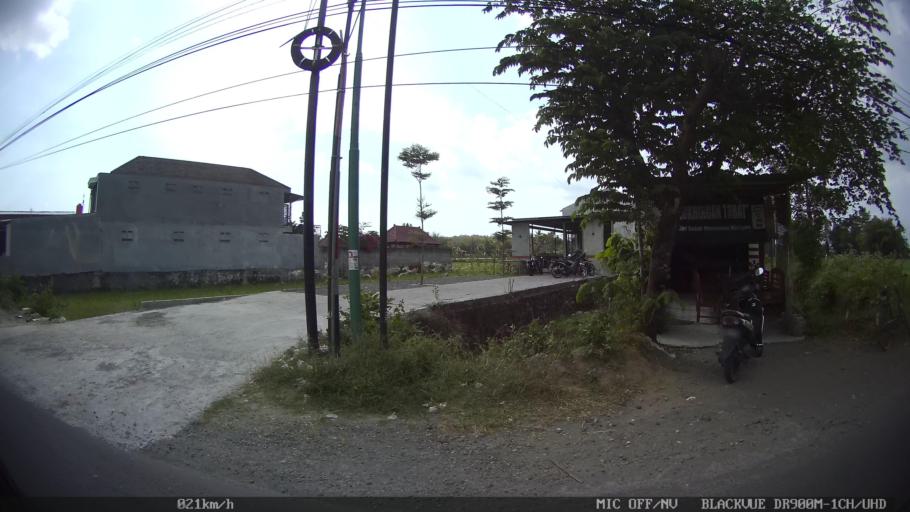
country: ID
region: Daerah Istimewa Yogyakarta
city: Kasihan
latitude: -7.8308
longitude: 110.3165
